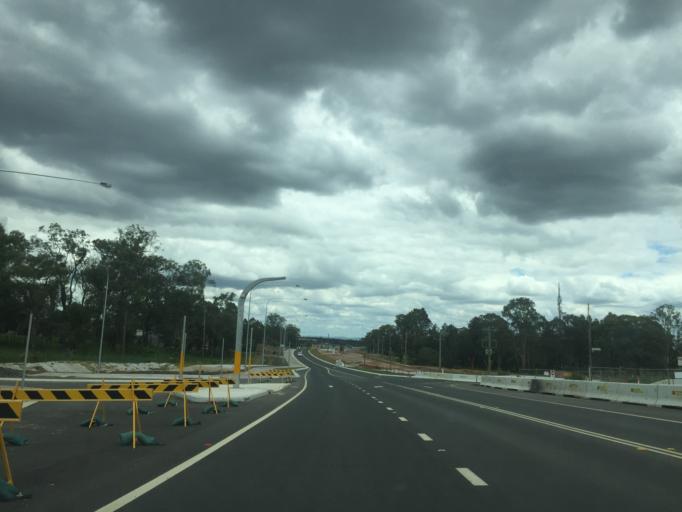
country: AU
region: New South Wales
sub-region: Blacktown
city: Riverstone
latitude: -33.6986
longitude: 150.8802
